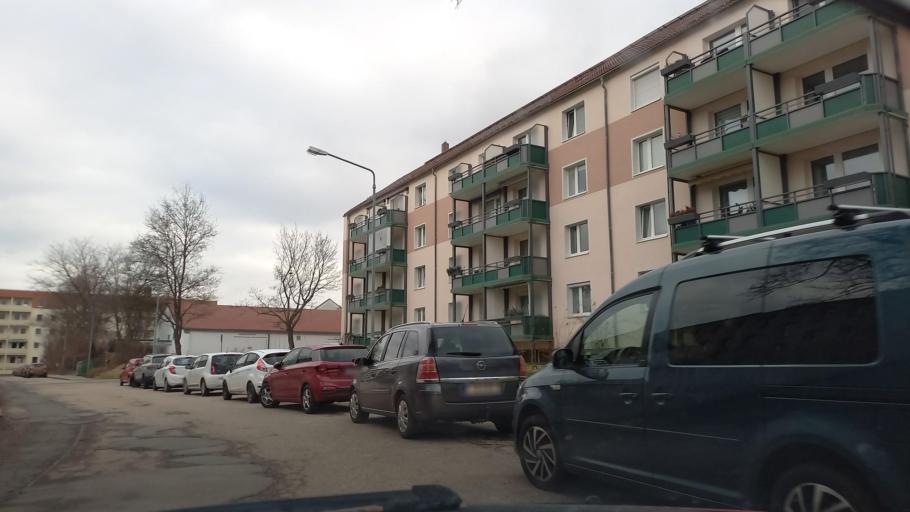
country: DE
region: Saxony
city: Wilkau-Hasslau
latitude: 50.6808
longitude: 12.5079
